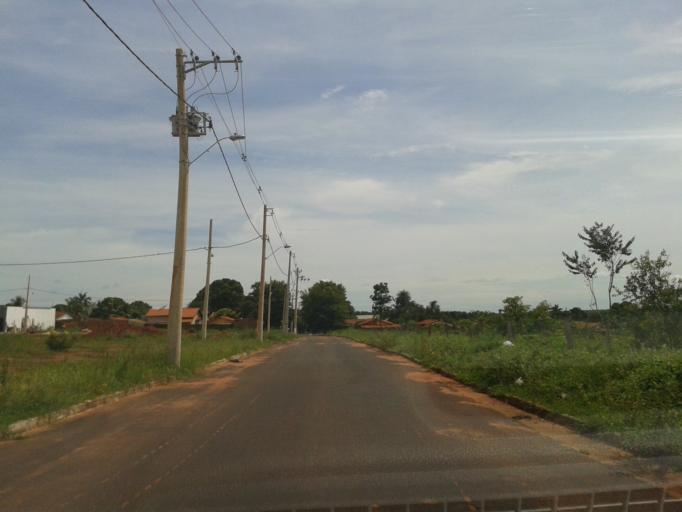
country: BR
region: Minas Gerais
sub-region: Santa Vitoria
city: Santa Vitoria
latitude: -18.8379
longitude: -50.1349
